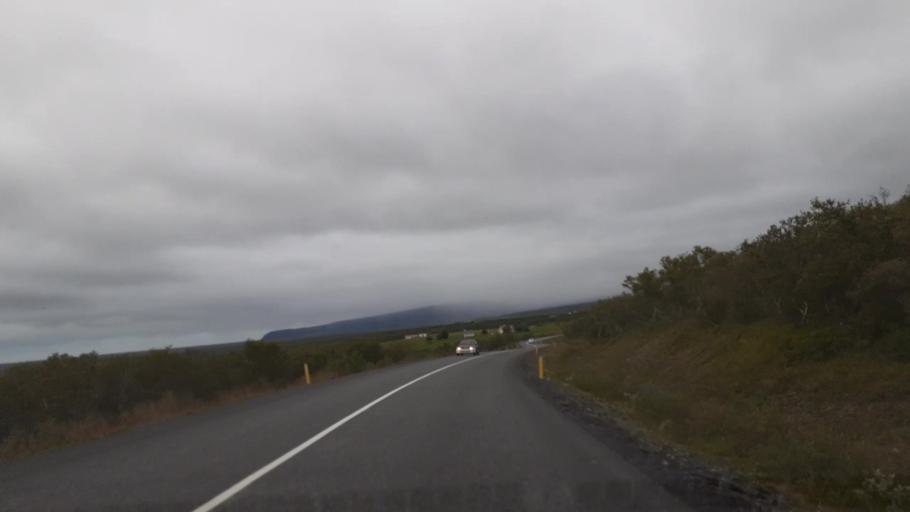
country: IS
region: Northeast
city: Husavik
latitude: 66.0619
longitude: -16.4449
